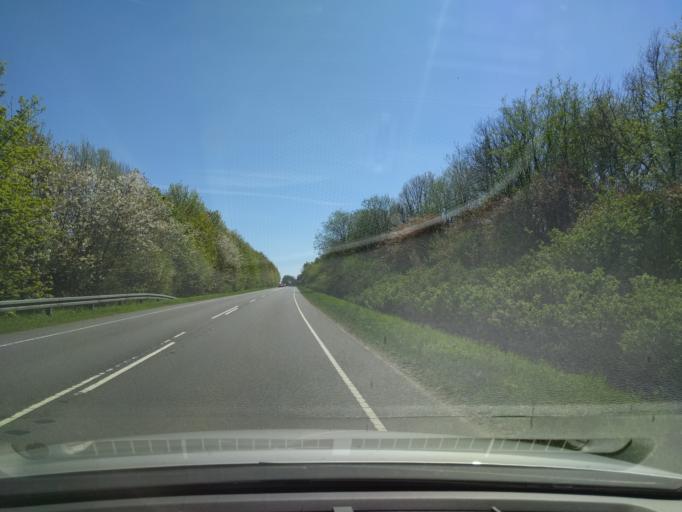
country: DK
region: South Denmark
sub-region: Vejen Kommune
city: Vejen
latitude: 55.5964
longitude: 9.1530
